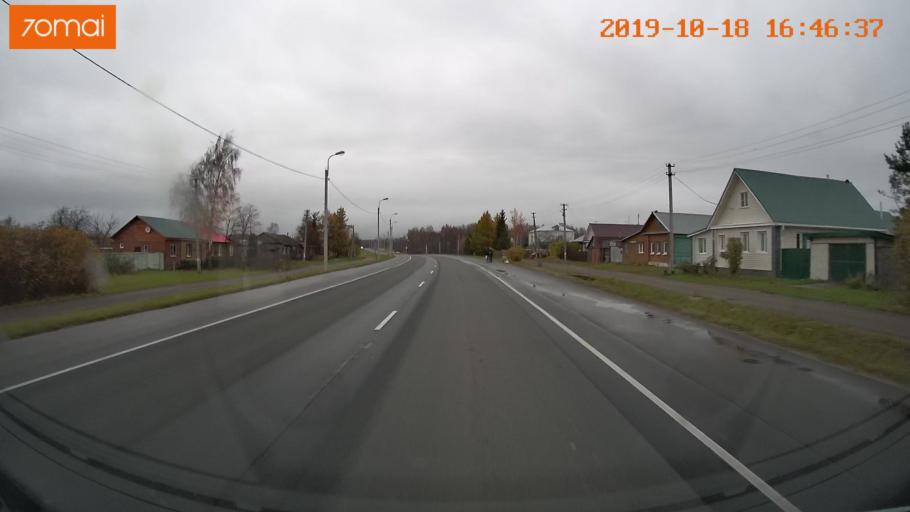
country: RU
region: Vladimir
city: Kideksha
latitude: 56.5192
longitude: 40.5547
